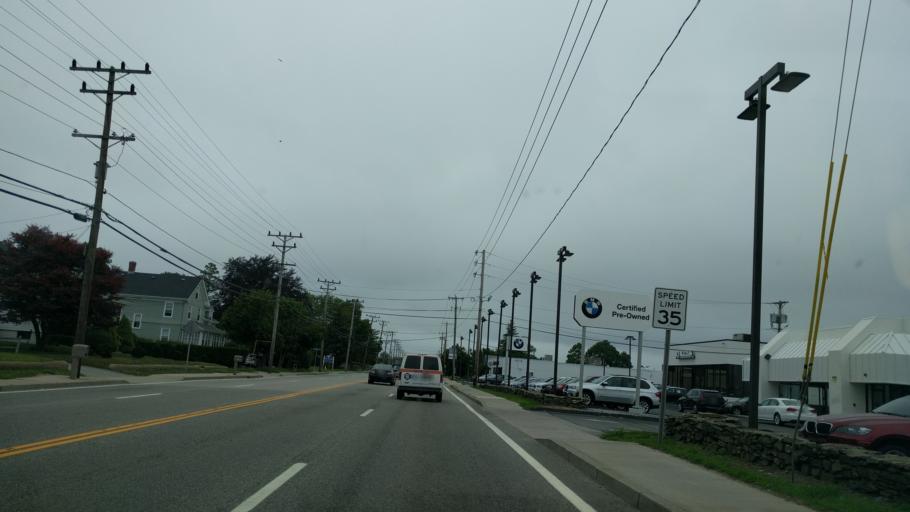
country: US
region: Rhode Island
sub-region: Newport County
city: Middletown
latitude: 41.5317
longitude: -71.2936
